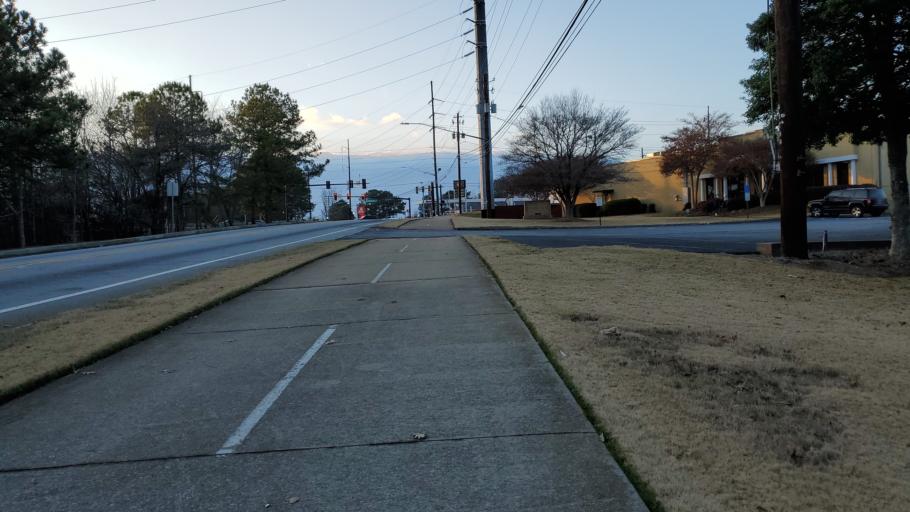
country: US
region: Georgia
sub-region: DeKalb County
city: Stone Mountain
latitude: 33.8256
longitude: -84.1944
